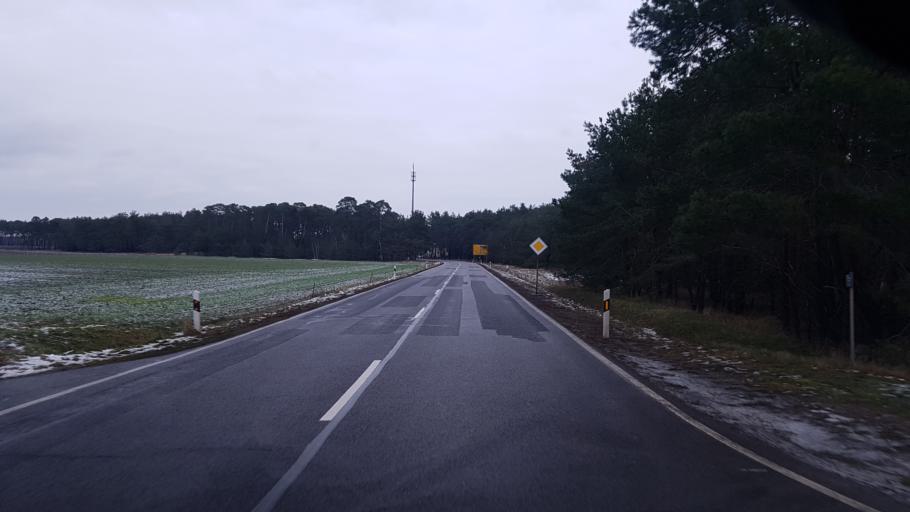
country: DE
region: Brandenburg
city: Heinersbruck
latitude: 51.8268
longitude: 14.5151
